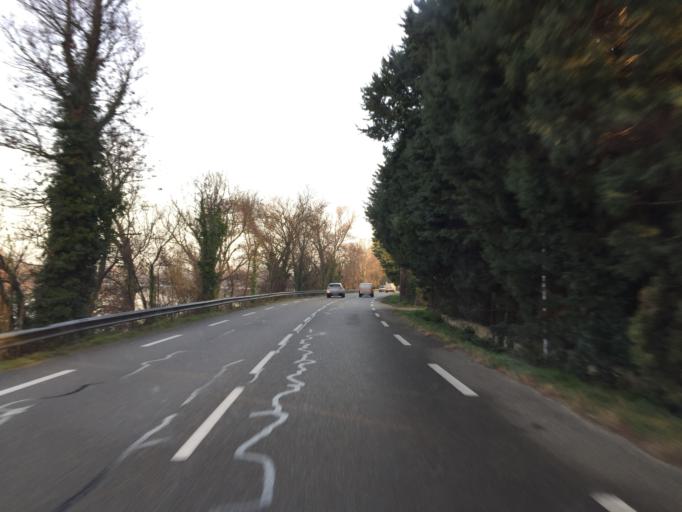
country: FR
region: Languedoc-Roussillon
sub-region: Departement du Gard
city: Montfaucon
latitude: 44.0824
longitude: 4.7611
